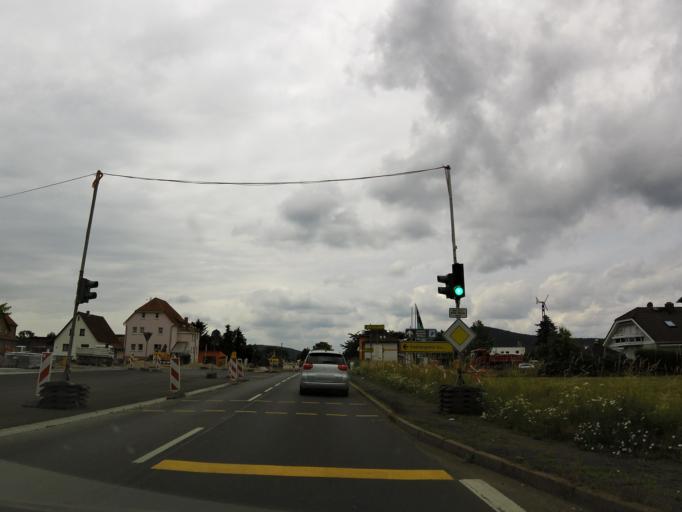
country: DE
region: Thuringia
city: Tiefenort
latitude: 50.8253
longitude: 10.1630
